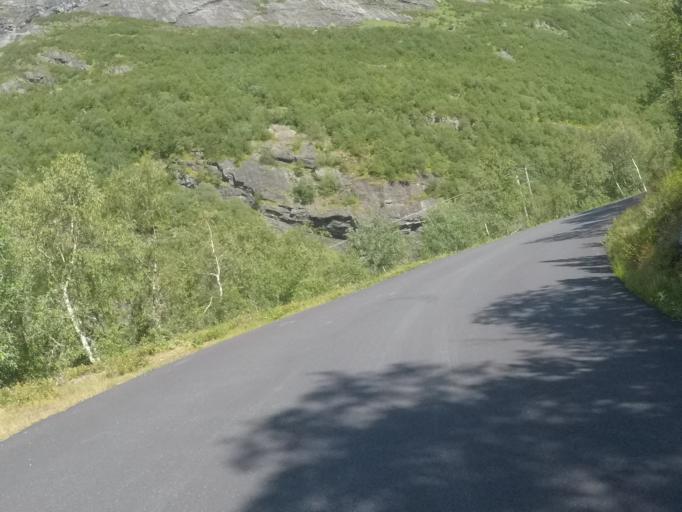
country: NO
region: More og Romsdal
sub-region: Norddal
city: Valldal
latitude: 61.9384
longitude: 7.2654
